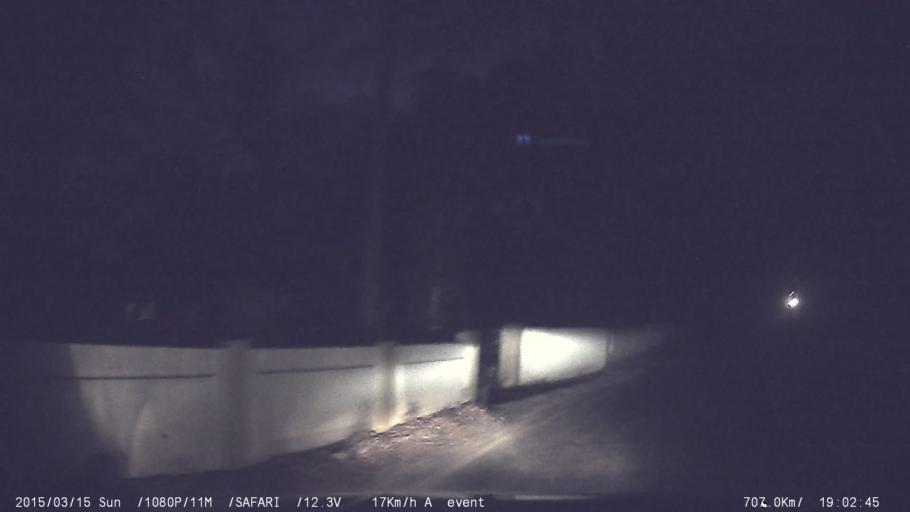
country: IN
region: Kerala
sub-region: Ernakulam
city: Muvattupuzha
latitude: 9.8780
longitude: 76.6477
